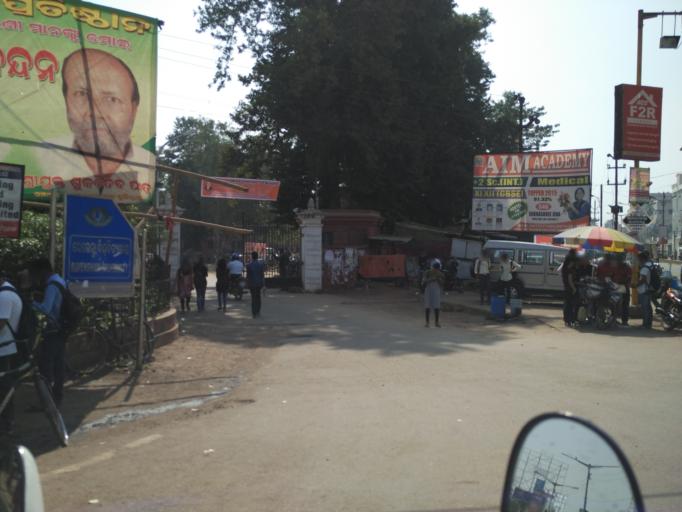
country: IN
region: Odisha
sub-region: Cuttack
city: Cuttack
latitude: 20.4668
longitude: 85.8945
